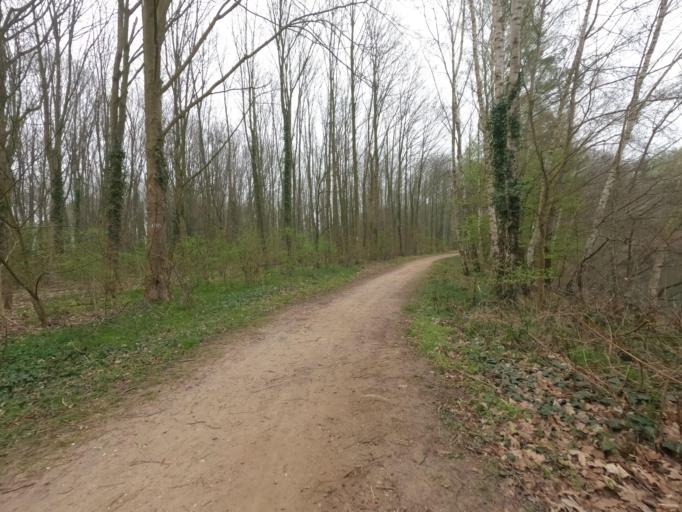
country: NL
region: Limburg
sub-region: Gemeente Roerdalen
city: Vlodrop
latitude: 51.1355
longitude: 6.0999
